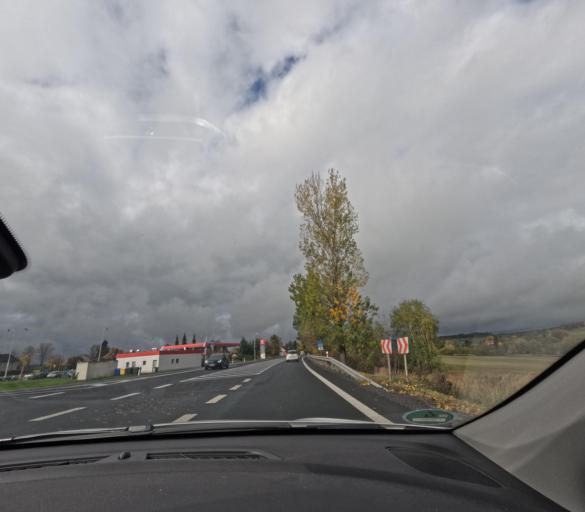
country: CZ
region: Karlovarsky
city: Bochov
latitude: 50.1494
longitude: 13.0534
